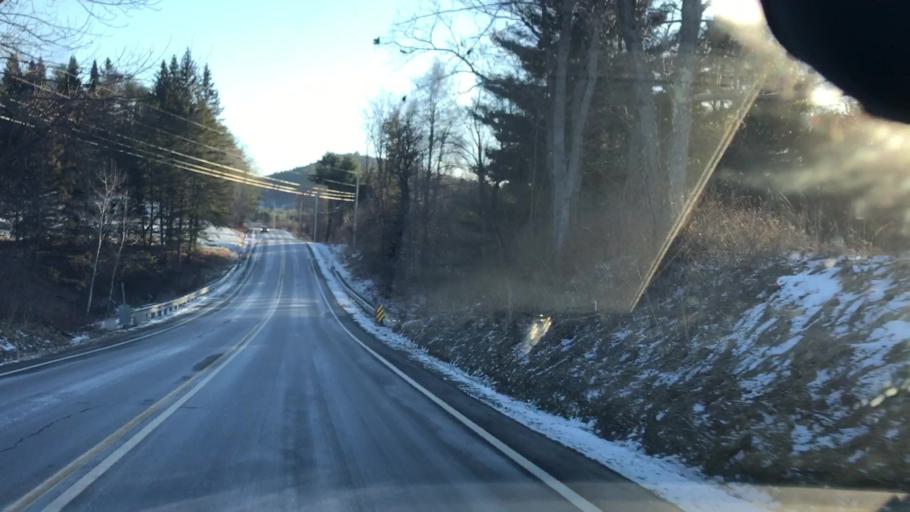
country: US
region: New Hampshire
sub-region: Grafton County
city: Lyme Town Offices
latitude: 43.8503
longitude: -72.1563
